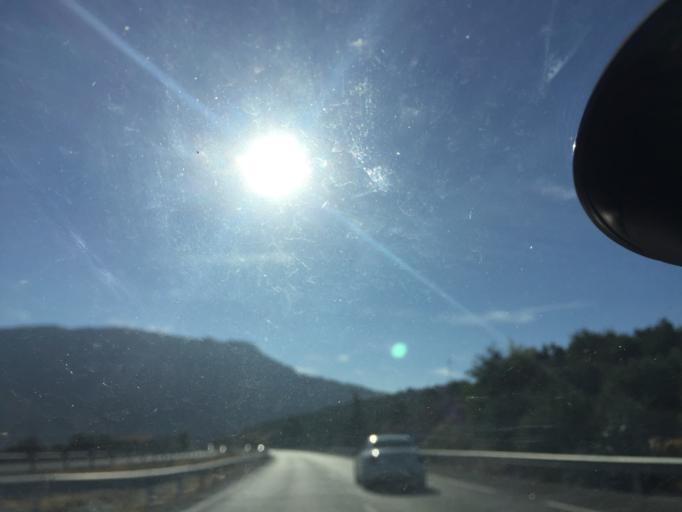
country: ES
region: Andalusia
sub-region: Provincia de Jaen
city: La Guardia de Jaen
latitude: 37.7533
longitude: -3.6981
